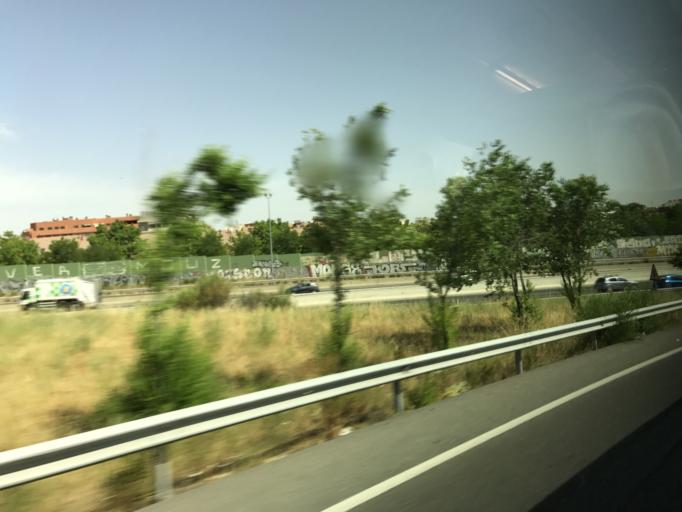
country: ES
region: Madrid
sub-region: Provincia de Madrid
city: Vicalvaro
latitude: 40.4149
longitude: -3.6170
